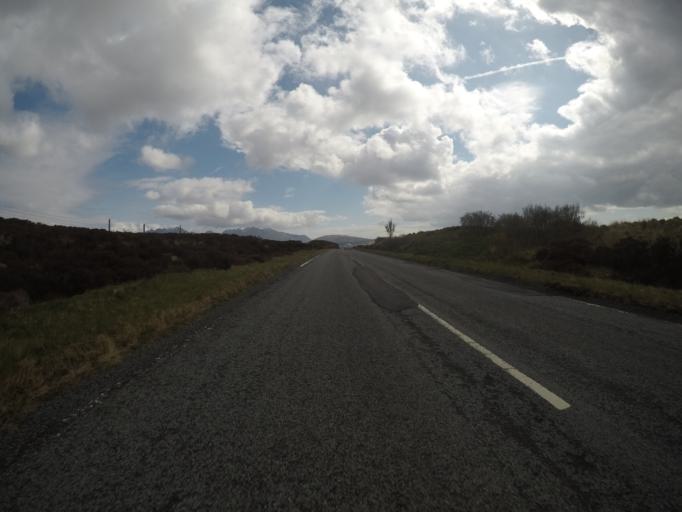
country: GB
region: Scotland
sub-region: Highland
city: Isle of Skye
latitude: 57.3148
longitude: -6.3201
